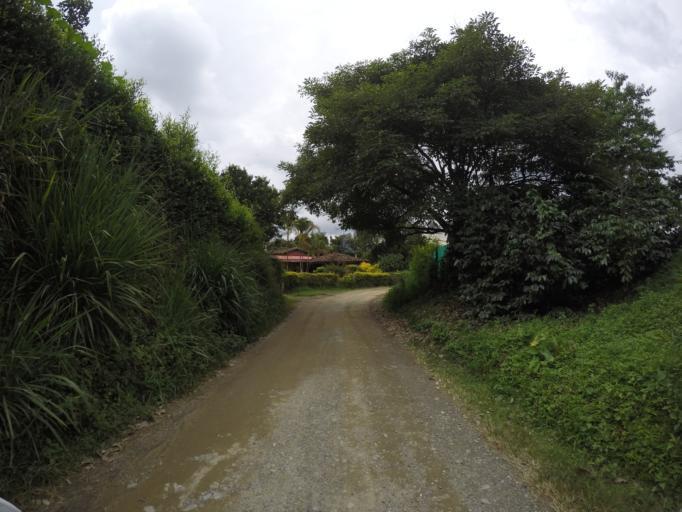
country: CO
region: Quindio
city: Circasia
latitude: 4.6212
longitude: -75.6931
